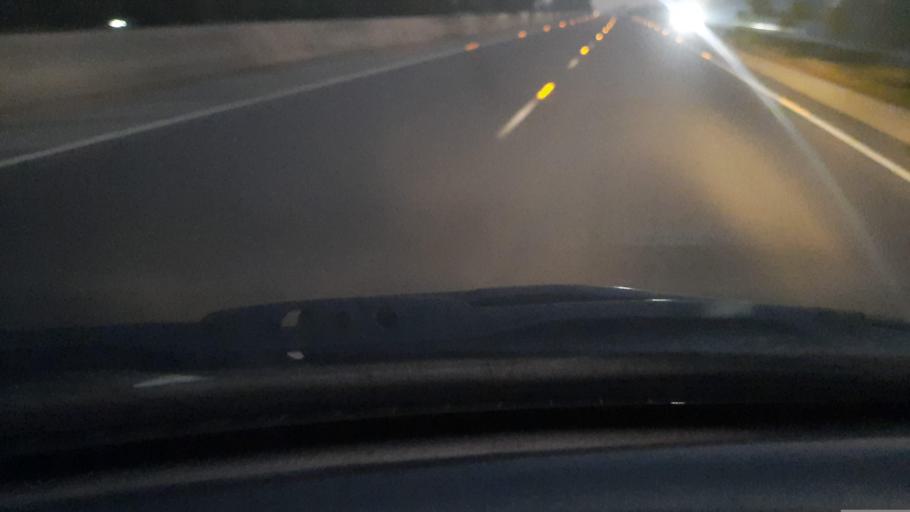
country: BD
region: Dhaka
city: Char Bhadrasan
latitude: 23.4000
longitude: 90.1787
